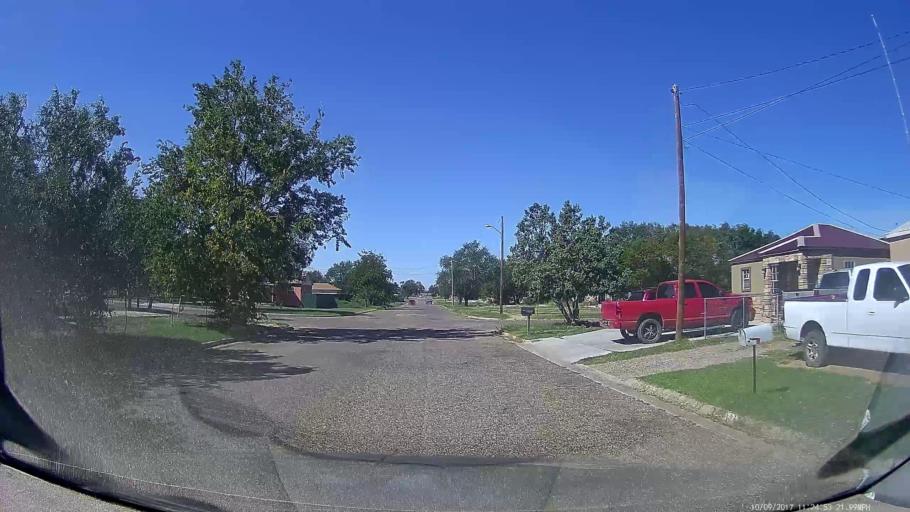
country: US
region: New Mexico
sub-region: Curry County
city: Clovis
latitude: 34.4110
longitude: -103.2180
